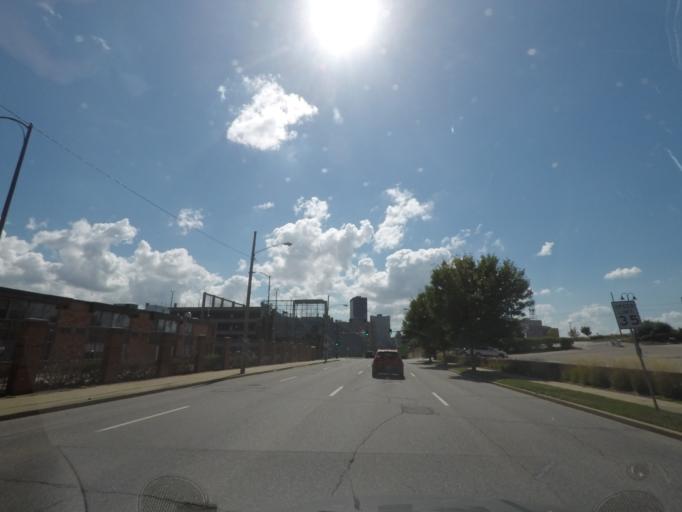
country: US
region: Iowa
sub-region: Polk County
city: Des Moines
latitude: 41.5941
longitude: -93.6269
